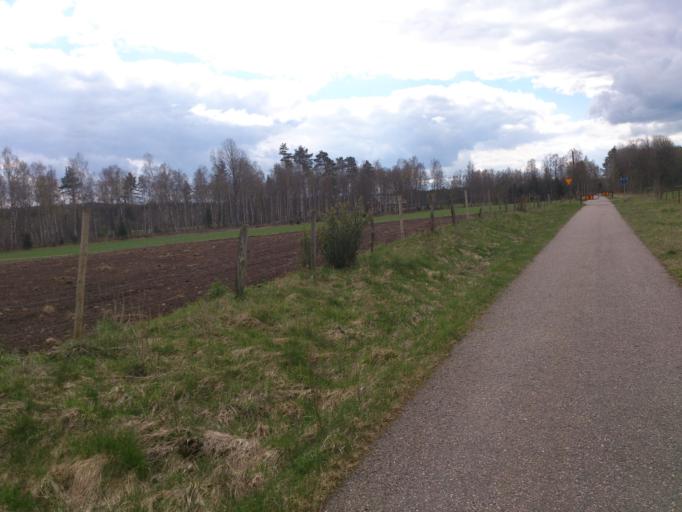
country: SE
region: Vaestra Goetaland
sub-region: Ulricehamns Kommun
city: Ulricehamn
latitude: 57.9566
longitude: 13.5099
